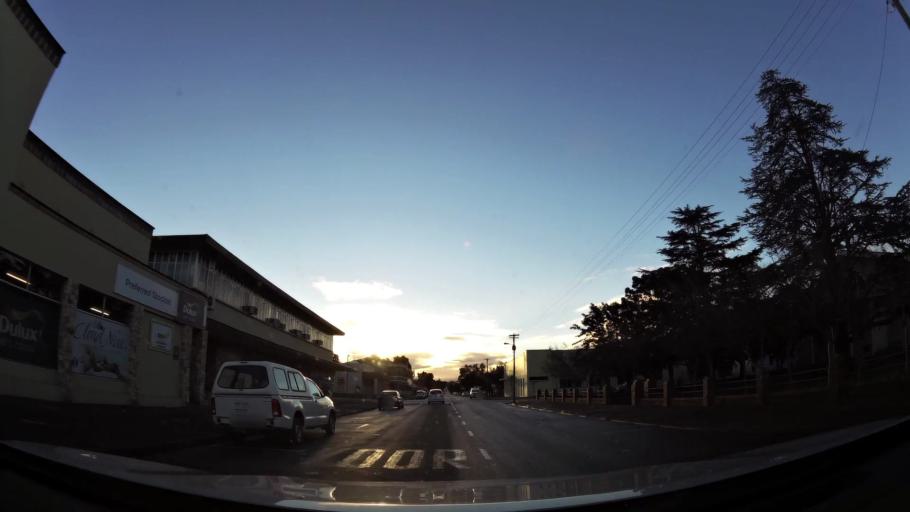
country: ZA
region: Western Cape
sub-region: Eden District Municipality
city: Riversdale
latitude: -34.0898
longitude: 20.9579
